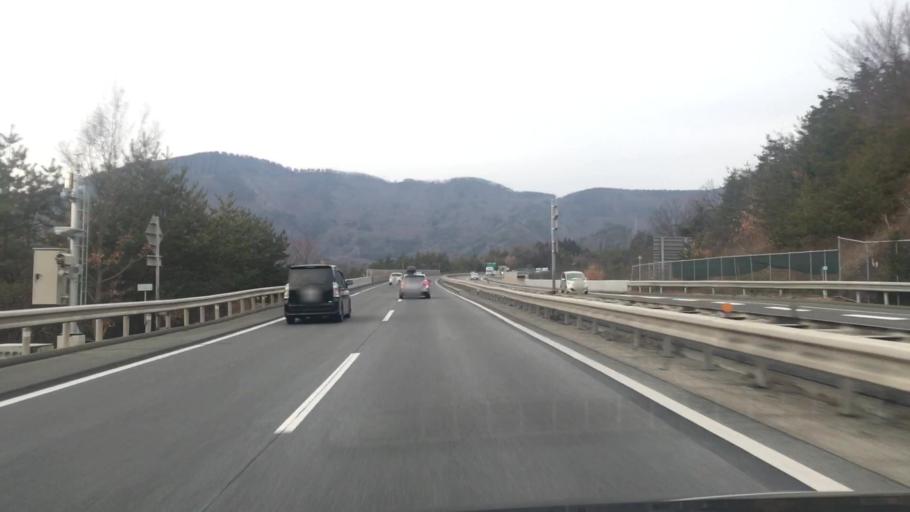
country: JP
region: Nagano
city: Ueda
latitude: 36.4590
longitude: 138.1994
